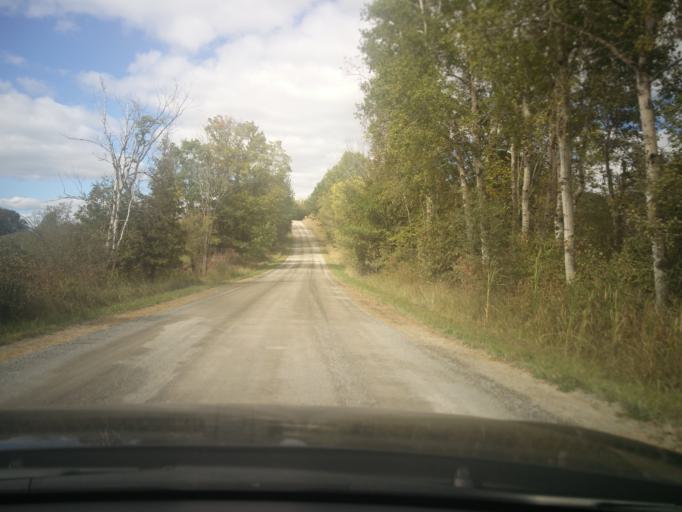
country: CA
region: Ontario
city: Perth
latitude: 44.6577
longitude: -76.5780
